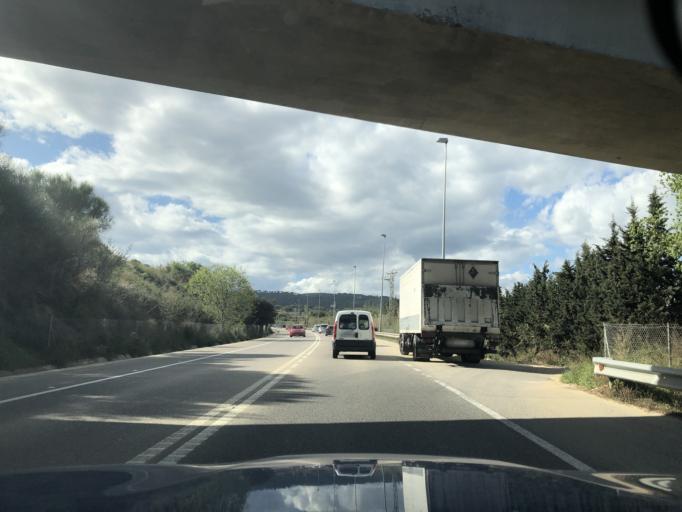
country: ES
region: Catalonia
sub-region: Provincia de Barcelona
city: Sant Andreu de Llavaneres
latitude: 41.5531
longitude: 2.4743
